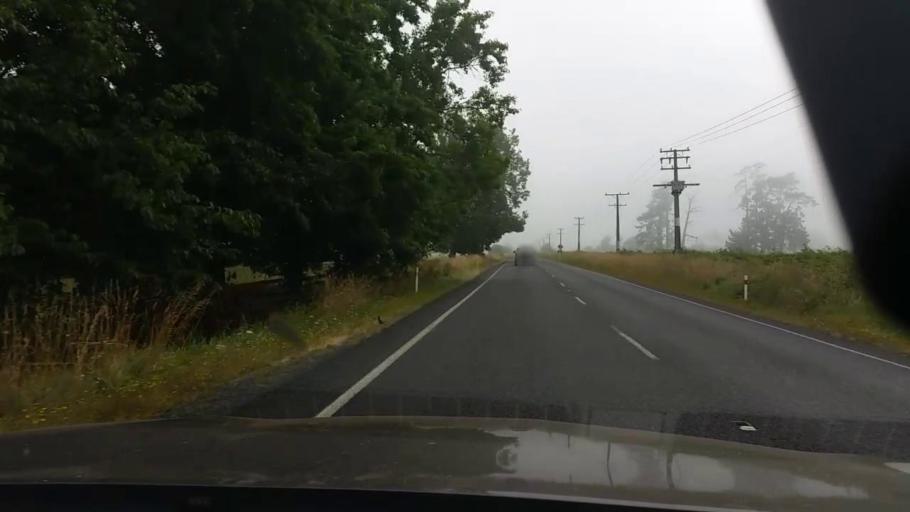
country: NZ
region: Waikato
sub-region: Waikato District
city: Ngaruawahia
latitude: -37.6376
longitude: 175.2976
